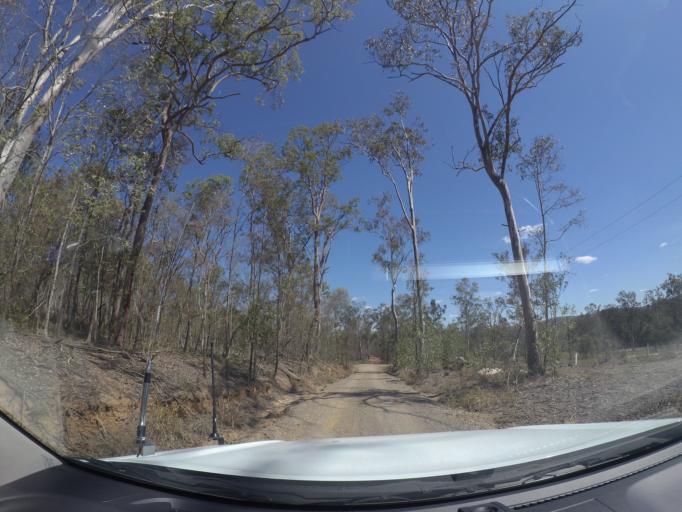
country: AU
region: Queensland
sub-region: Logan
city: North Maclean
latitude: -27.7754
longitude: 152.9371
